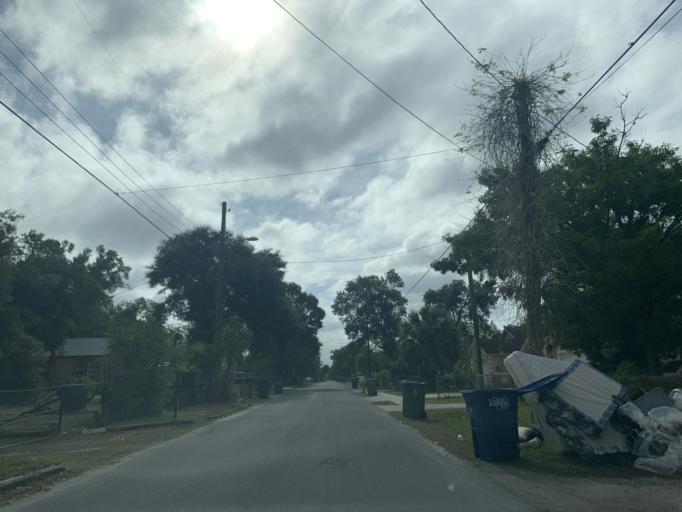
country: US
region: Florida
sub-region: Hillsborough County
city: East Lake-Orient Park
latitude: 27.9776
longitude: -82.3986
